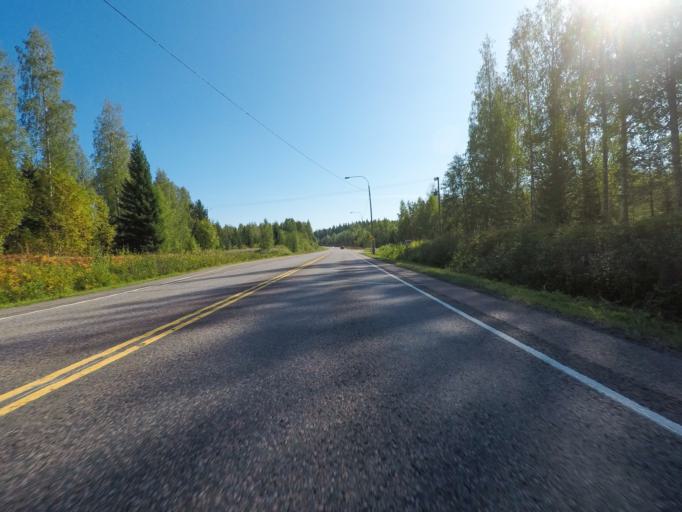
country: FI
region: Northern Savo
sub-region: Varkaus
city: Leppaevirta
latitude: 62.4573
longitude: 27.7863
